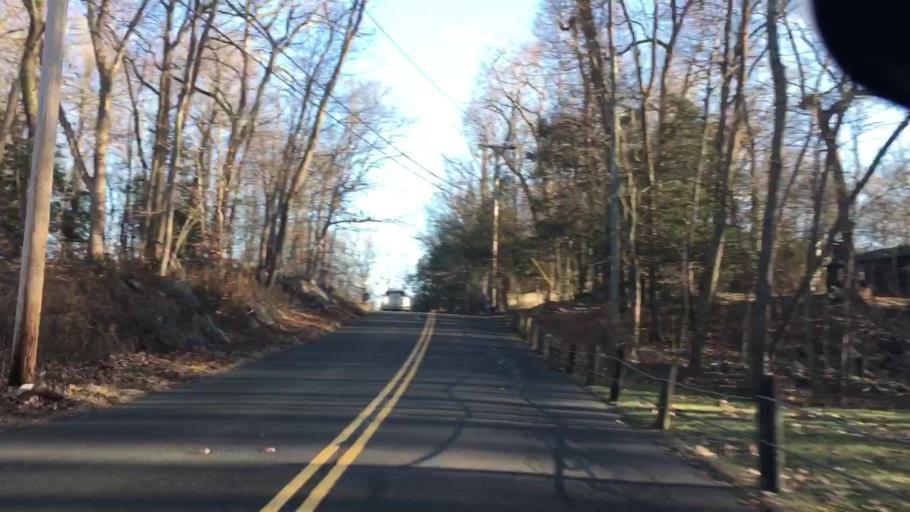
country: US
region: Connecticut
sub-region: Fairfield County
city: Newtown
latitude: 41.4697
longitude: -73.3404
